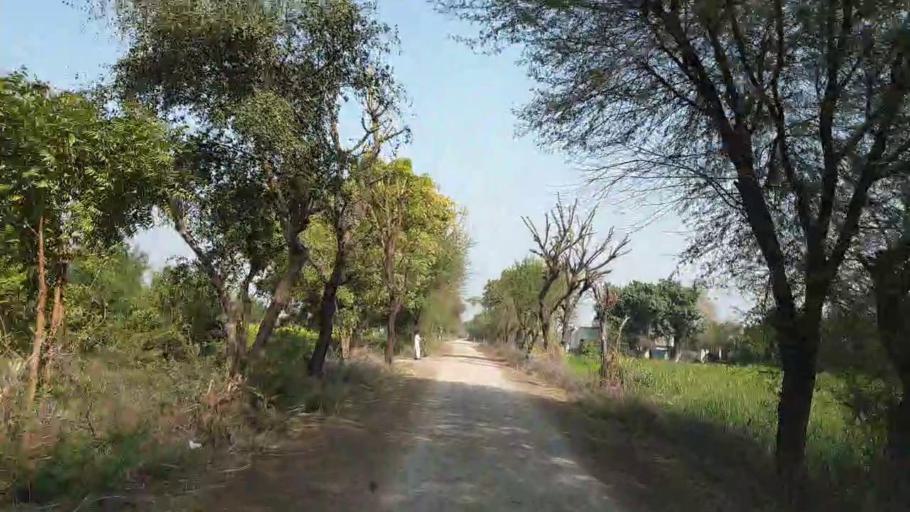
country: PK
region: Sindh
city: Mirpur Khas
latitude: 25.5834
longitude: 69.0126
